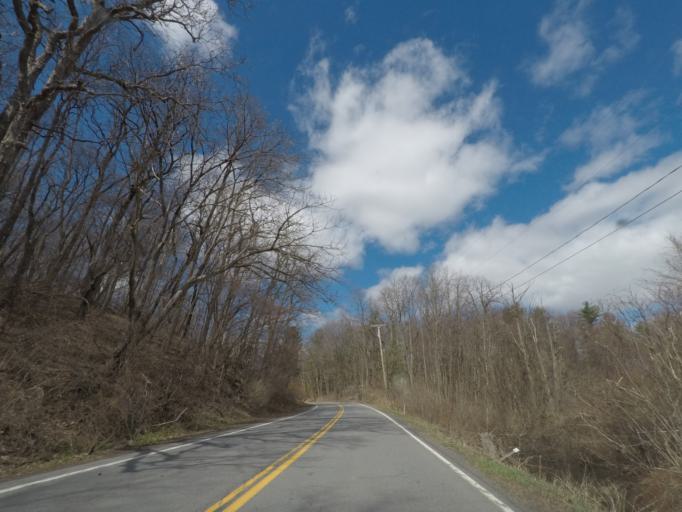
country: US
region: New York
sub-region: Albany County
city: Voorheesville
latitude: 42.6556
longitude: -73.9877
